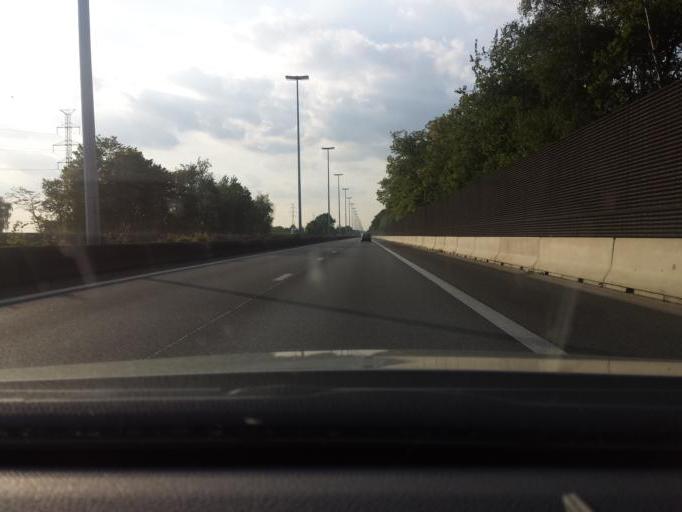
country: BE
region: Flanders
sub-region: Provincie Limburg
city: Hasselt
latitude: 50.9267
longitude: 5.3096
